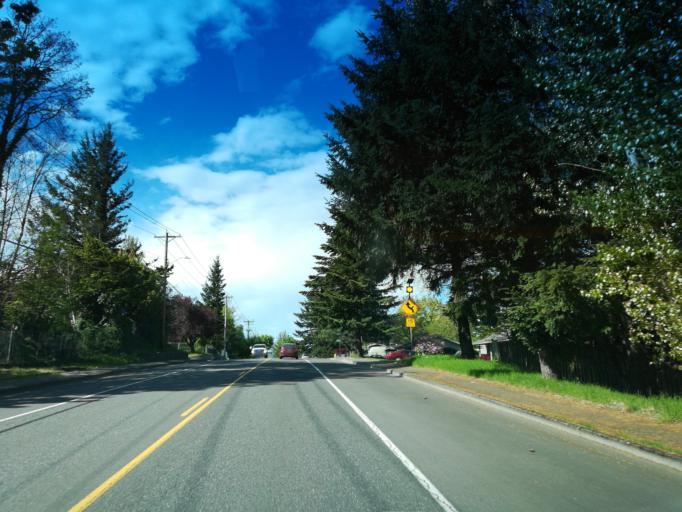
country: US
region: Oregon
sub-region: Multnomah County
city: Troutdale
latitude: 45.5317
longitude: -122.3874
